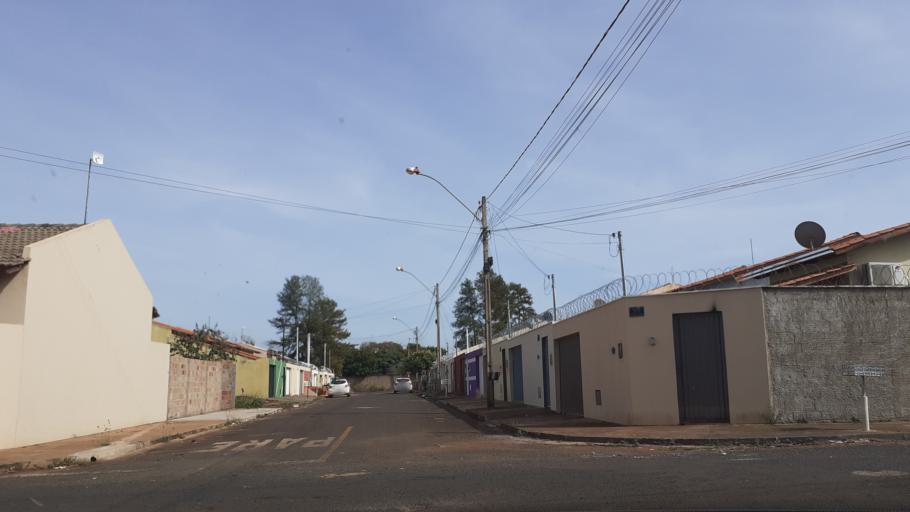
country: BR
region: Goias
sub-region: Itumbiara
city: Itumbiara
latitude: -18.4235
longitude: -49.2447
